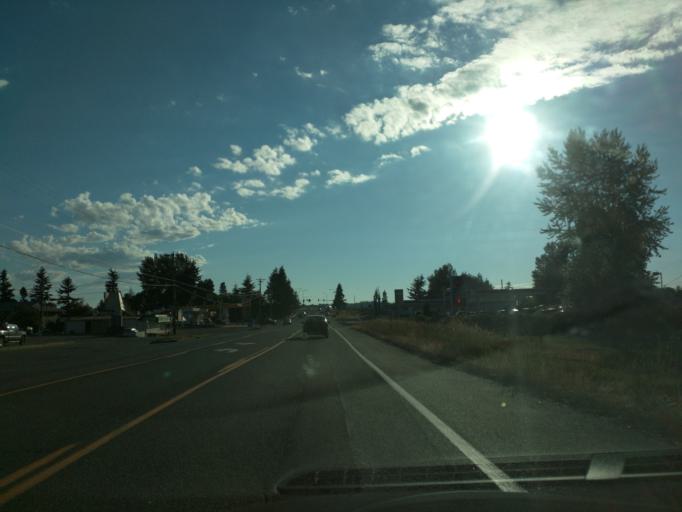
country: US
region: Washington
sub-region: Snohomish County
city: Smokey Point
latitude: 48.1881
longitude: -122.1973
